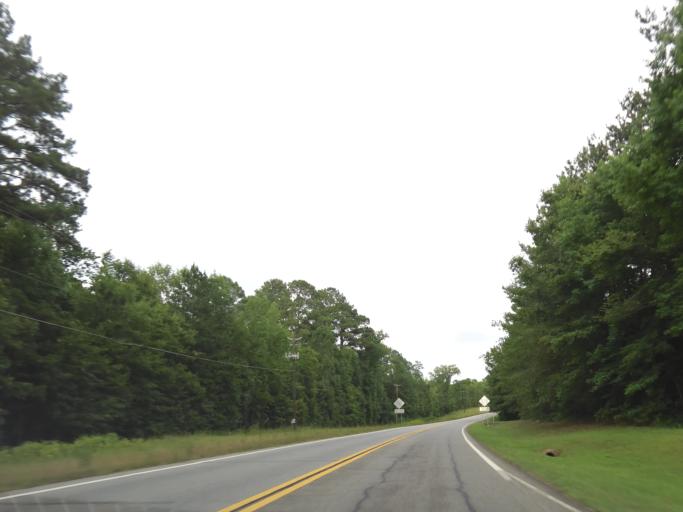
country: US
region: Georgia
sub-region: Bibb County
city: West Point
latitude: 32.8642
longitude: -83.8100
